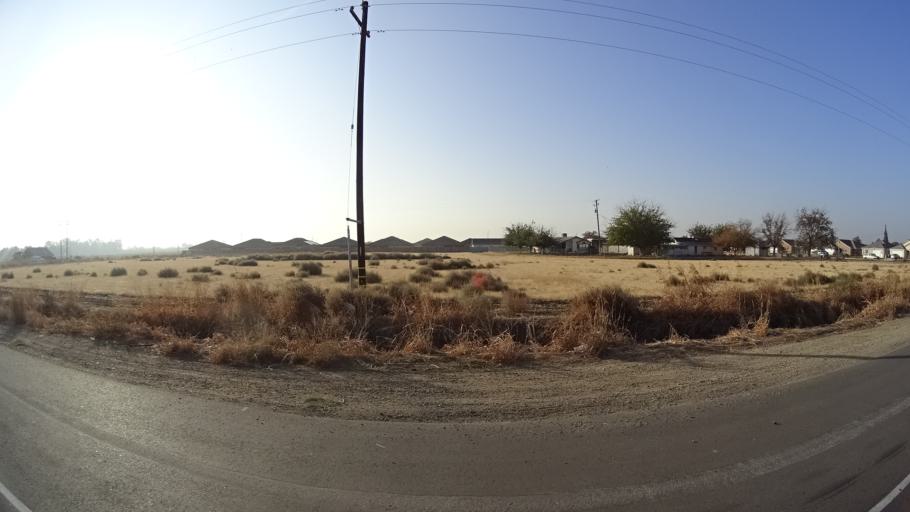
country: US
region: California
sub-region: Kern County
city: Greenfield
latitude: 35.2669
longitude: -119.0132
